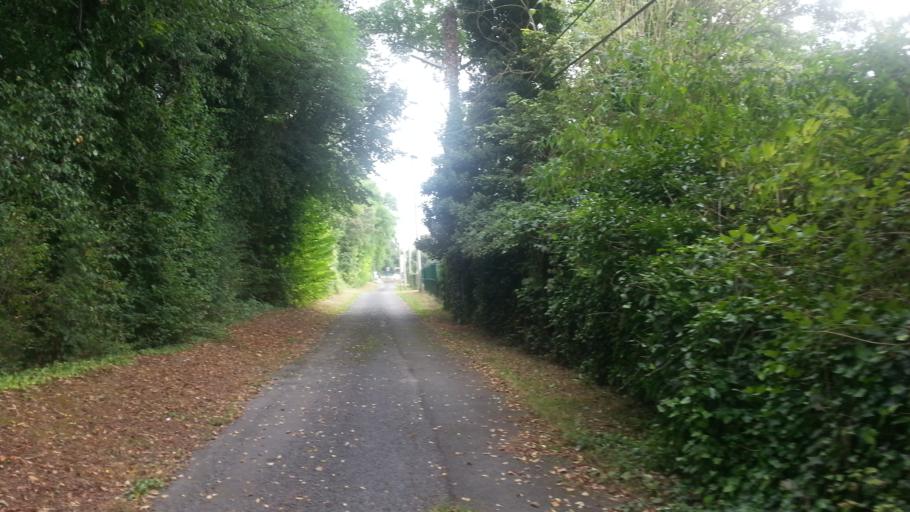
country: FR
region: Picardie
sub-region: Departement de l'Oise
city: Saint-Maximin
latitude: 49.2187
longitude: 2.4494
